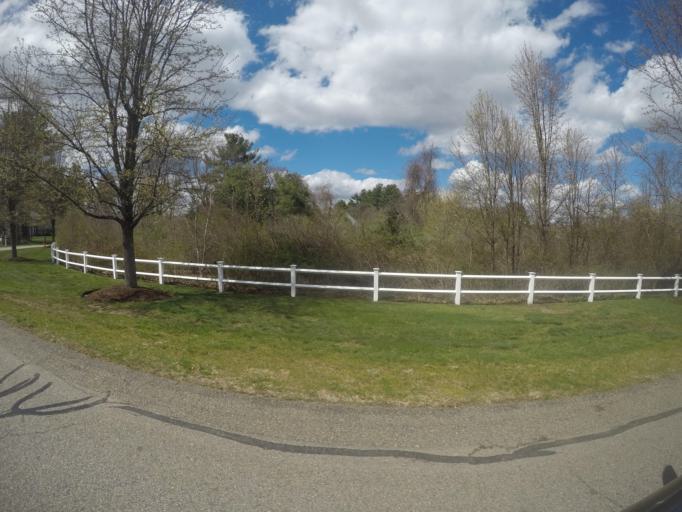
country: US
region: Massachusetts
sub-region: Plymouth County
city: West Bridgewater
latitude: 42.0193
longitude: -71.0678
